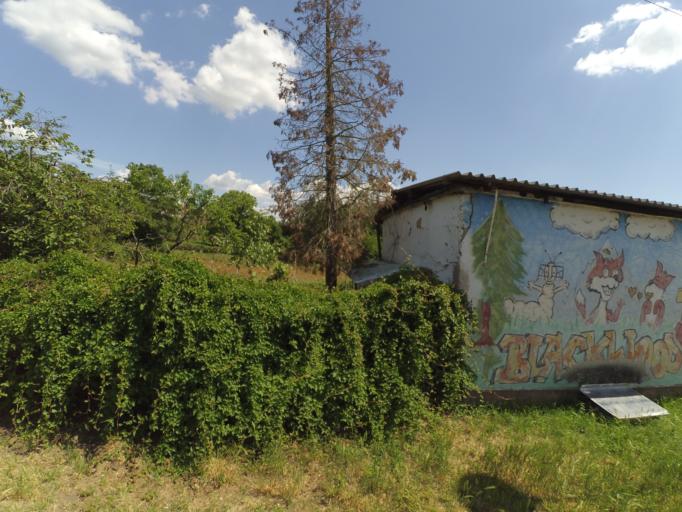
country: DE
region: Baden-Wuerttemberg
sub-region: Karlsruhe Region
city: Bruhl
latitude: 49.4130
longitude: 8.5245
